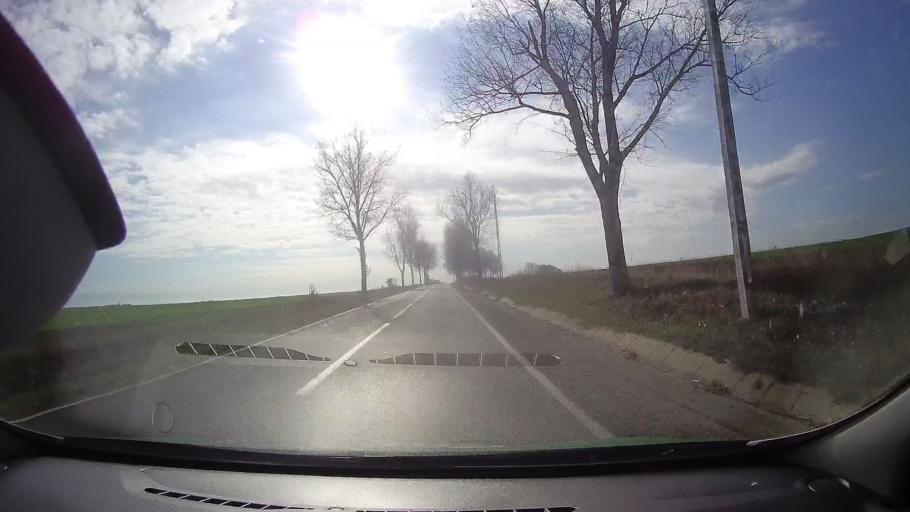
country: RO
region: Tulcea
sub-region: Comuna Valea Nucarilor
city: Agighiol
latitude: 44.9988
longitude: 28.8863
